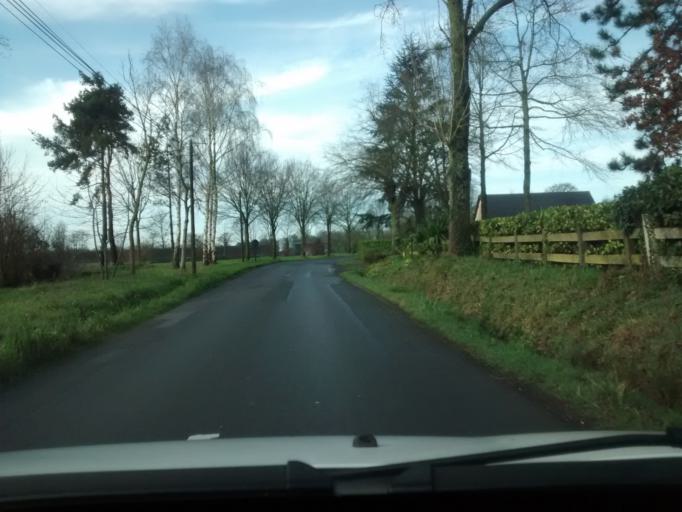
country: FR
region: Brittany
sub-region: Departement d'Ille-et-Vilaine
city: Montgermont
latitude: 48.1454
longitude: -1.7419
